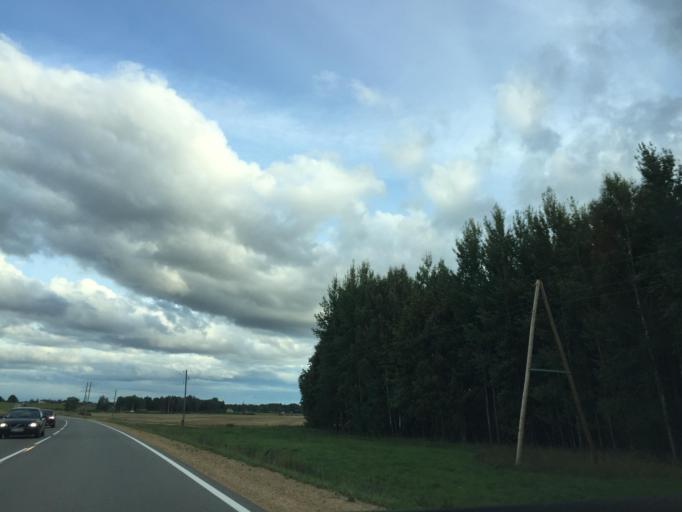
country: LV
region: Nereta
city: Nereta
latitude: 56.2216
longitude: 25.2849
